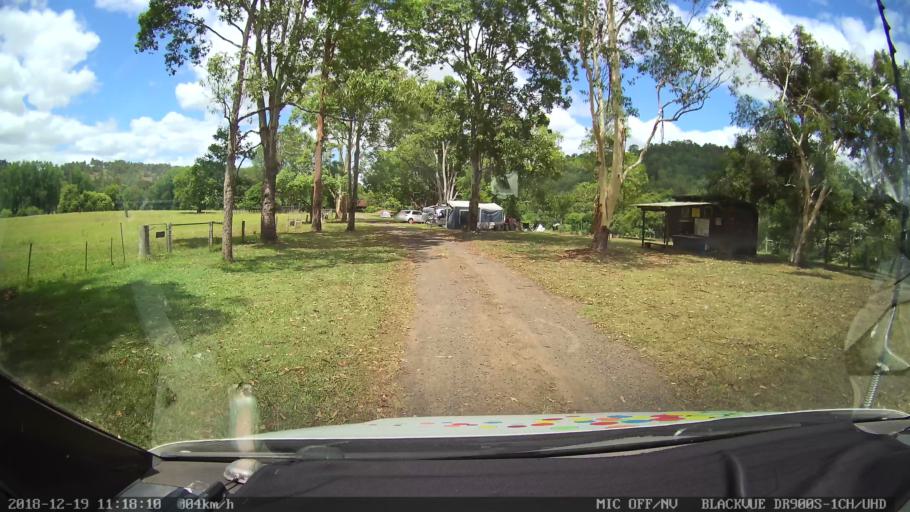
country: AU
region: New South Wales
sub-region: Lismore Municipality
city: Nimbin
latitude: -28.6784
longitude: 153.2790
